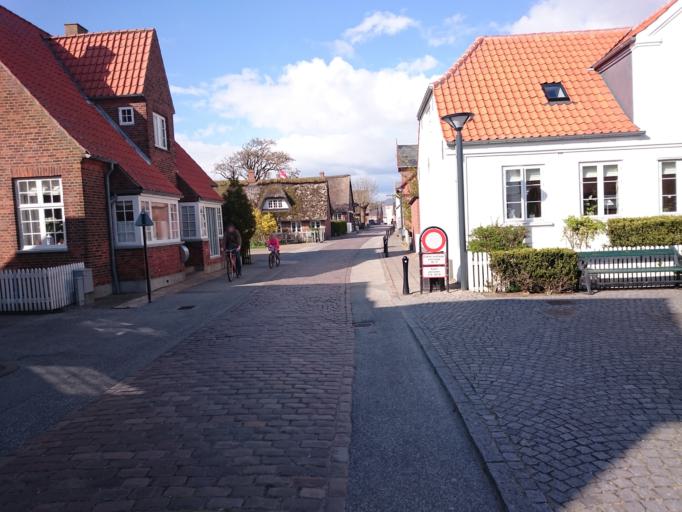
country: DK
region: South Denmark
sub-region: Fano Kommune
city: Nordby
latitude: 55.4459
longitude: 8.4048
